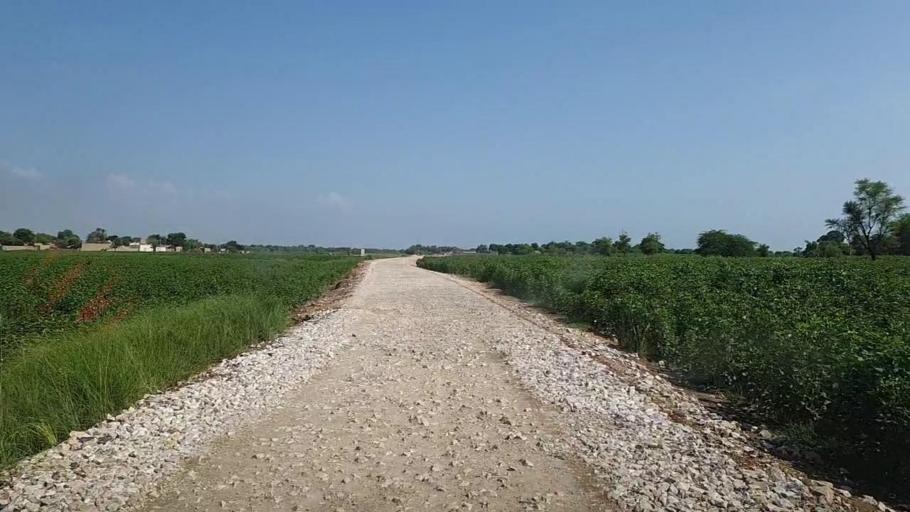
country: PK
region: Sindh
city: Bhiria
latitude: 26.8748
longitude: 68.2314
